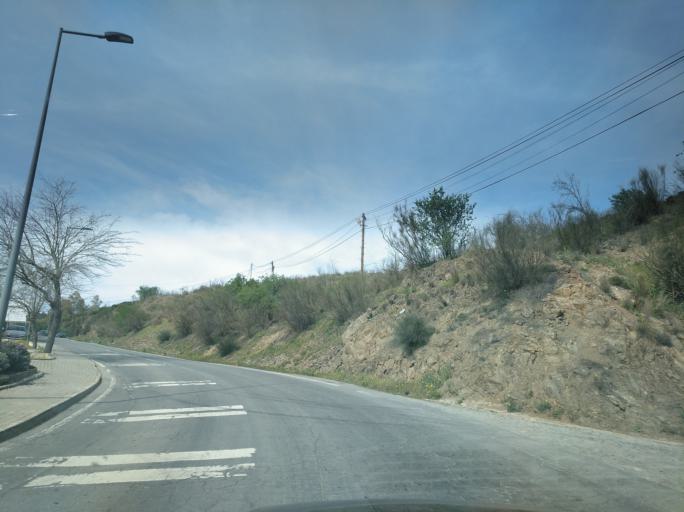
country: PT
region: Beja
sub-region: Mertola
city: Mertola
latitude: 37.6443
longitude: -7.6591
